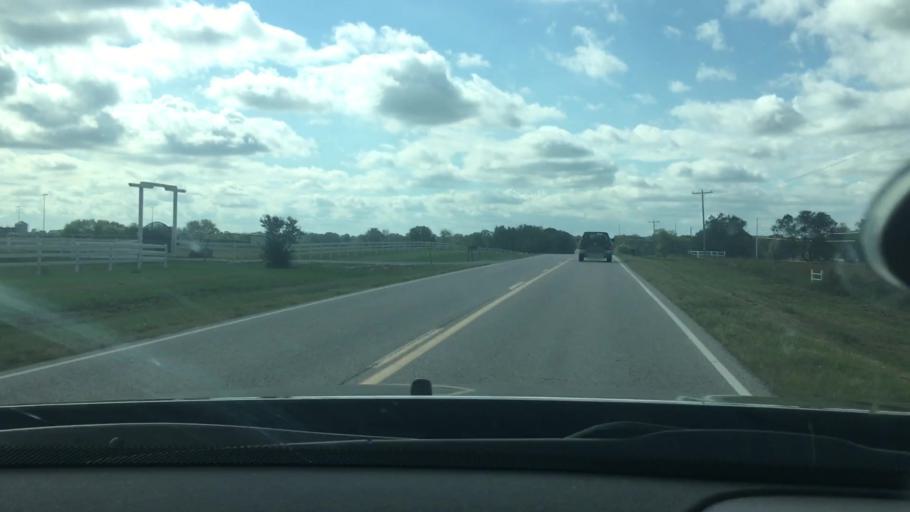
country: US
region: Oklahoma
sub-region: Pontotoc County
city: Ada
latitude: 34.7132
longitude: -96.6349
